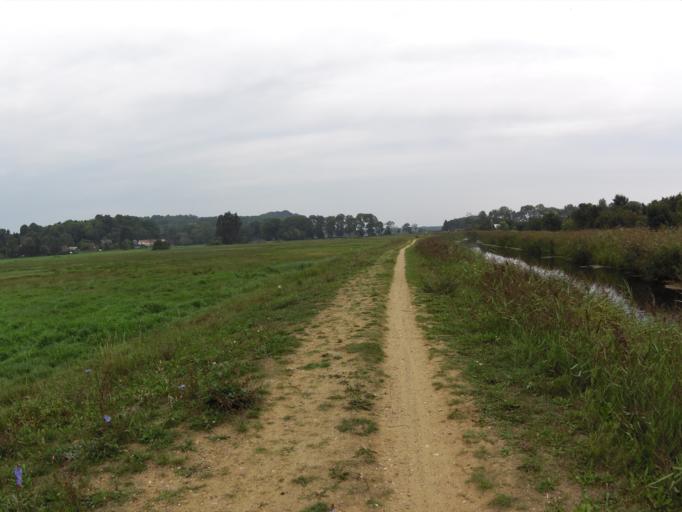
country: PL
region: West Pomeranian Voivodeship
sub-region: Swinoujscie
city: Swinoujscie
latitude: 53.8741
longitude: 14.2136
